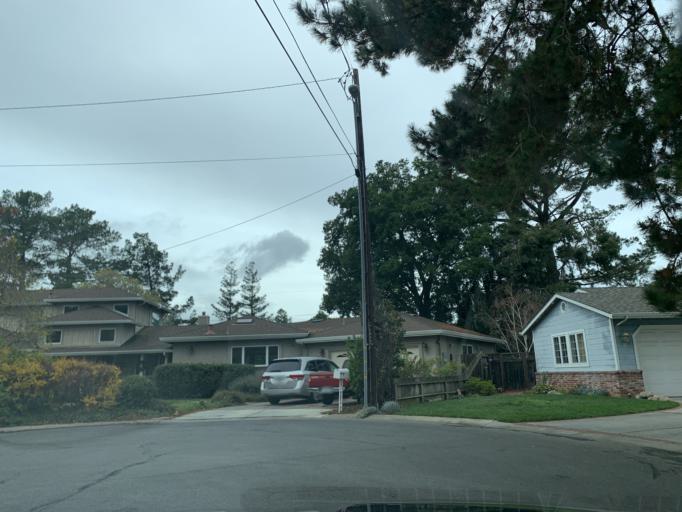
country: US
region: California
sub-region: Santa Clara County
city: Cupertino
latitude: 37.3275
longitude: -122.0580
